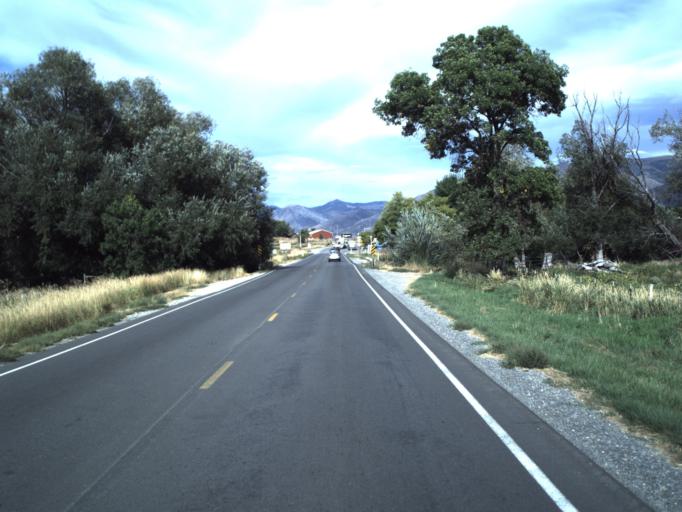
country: US
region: Utah
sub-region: Cache County
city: Wellsville
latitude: 41.6429
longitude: -111.9181
